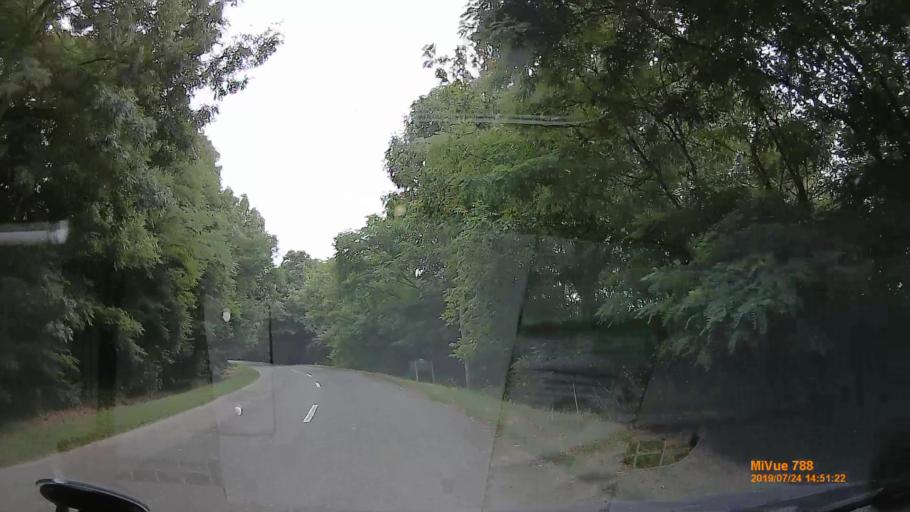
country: HU
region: Szabolcs-Szatmar-Bereg
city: Aranyosapati
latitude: 48.2730
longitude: 22.2844
